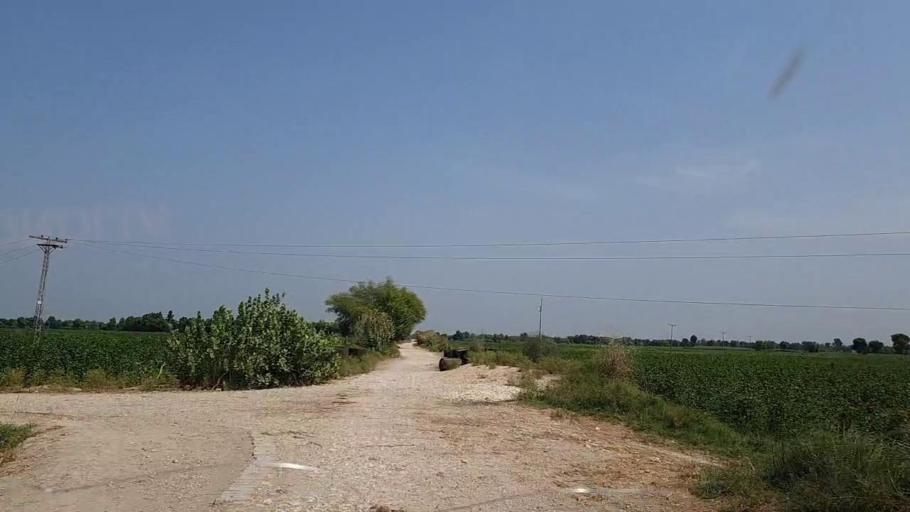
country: PK
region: Sindh
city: Adilpur
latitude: 27.8383
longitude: 69.2797
